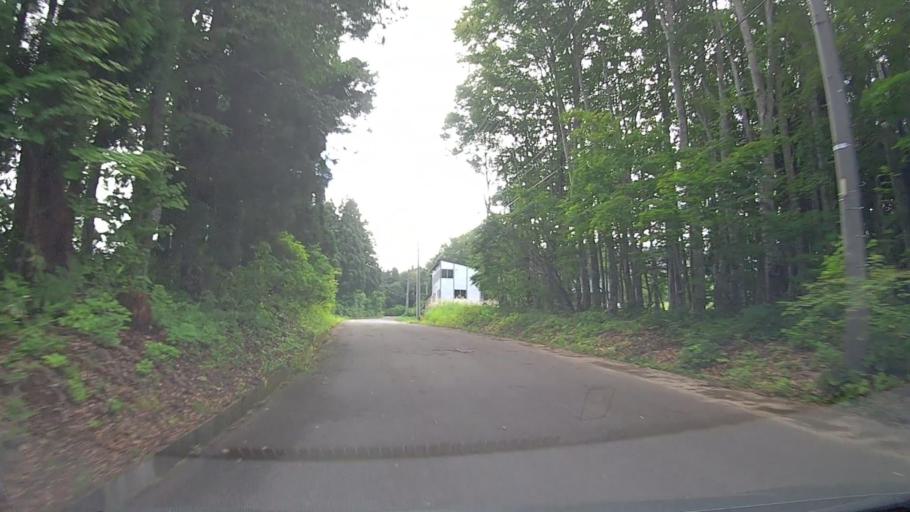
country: JP
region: Nagano
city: Iiyama
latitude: 36.9189
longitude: 138.4816
